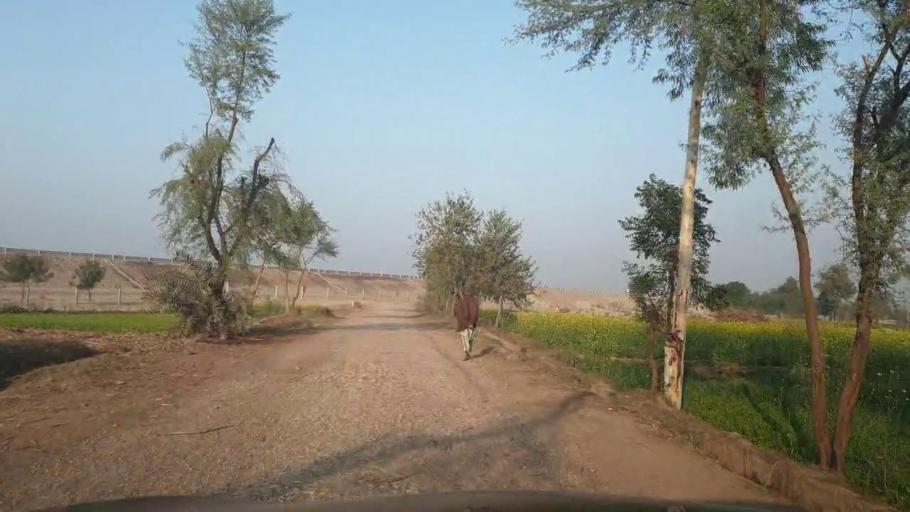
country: PK
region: Sindh
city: Ubauro
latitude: 28.3221
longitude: 69.7751
